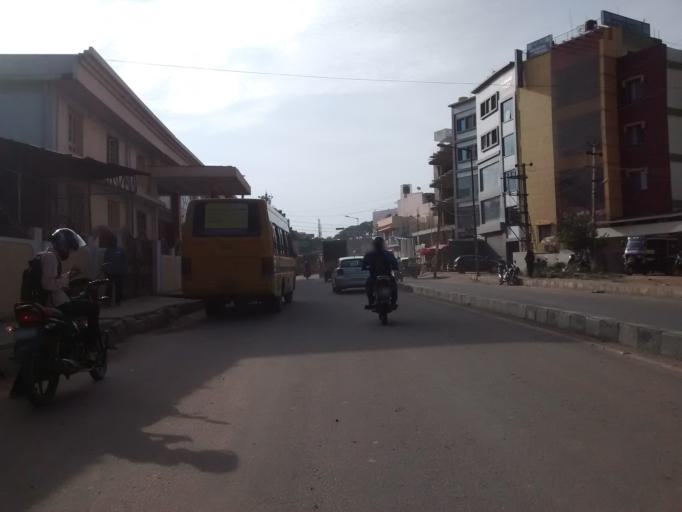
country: IN
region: Karnataka
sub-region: Bangalore Urban
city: Yelahanka
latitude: 13.0984
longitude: 77.5982
